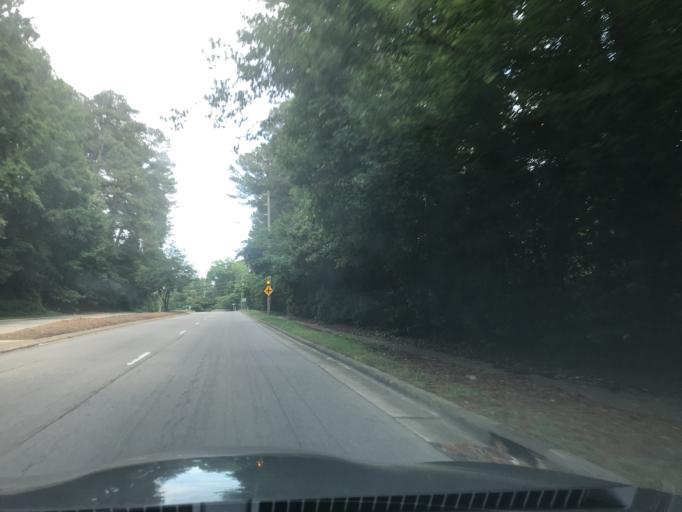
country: US
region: North Carolina
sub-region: Wake County
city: West Raleigh
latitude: 35.8614
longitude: -78.6916
